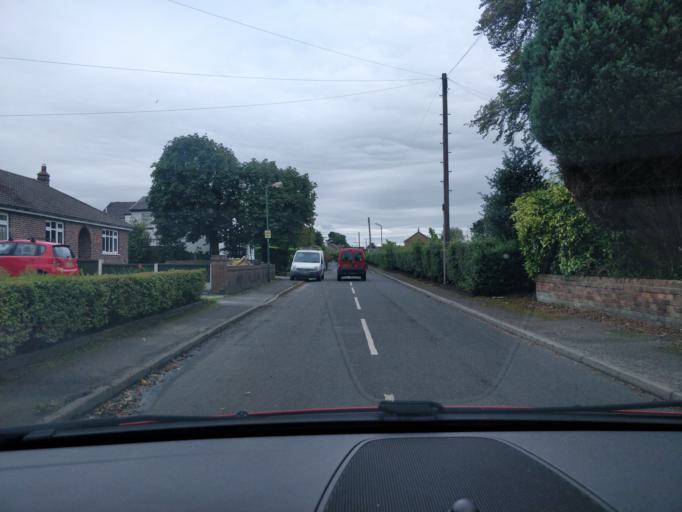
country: GB
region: England
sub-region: Lancashire
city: Ormskirk
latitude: 53.6114
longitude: -2.8421
